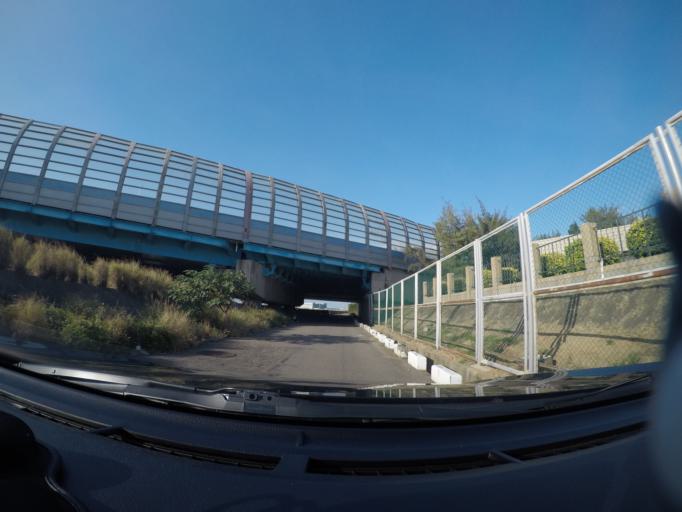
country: TW
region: Taiwan
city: Taoyuan City
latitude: 25.0985
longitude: 121.2515
